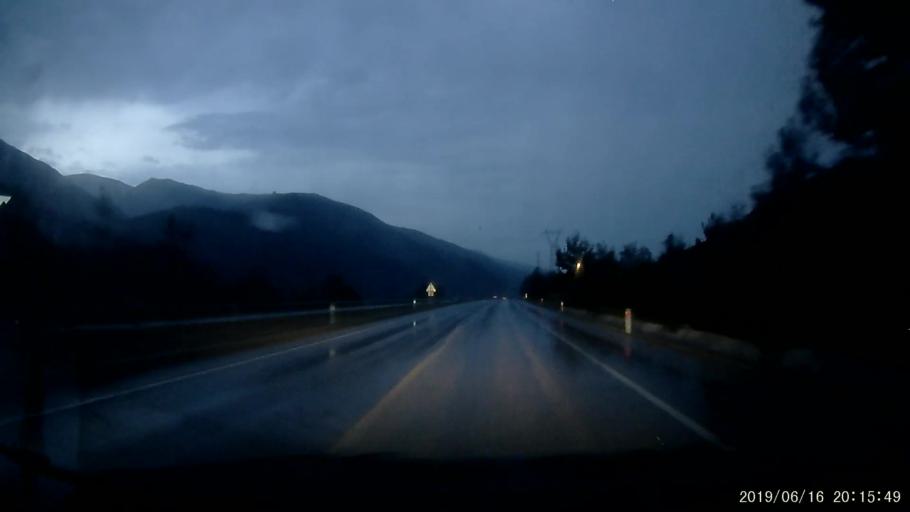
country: TR
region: Tokat
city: Resadiye
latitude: 40.3561
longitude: 37.4555
